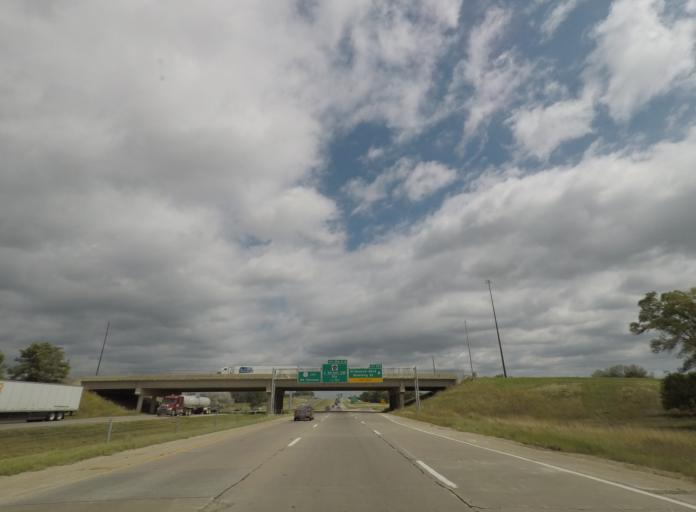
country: US
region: Iowa
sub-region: Linn County
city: Cedar Rapids
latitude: 41.9268
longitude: -91.6579
